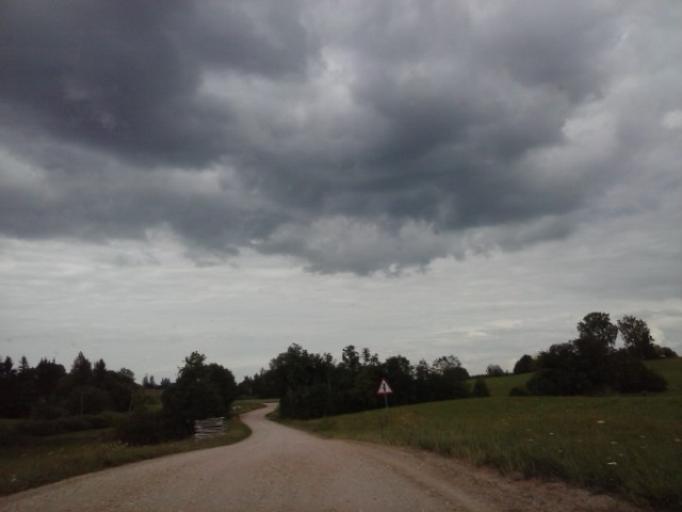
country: EE
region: Vorumaa
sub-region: Voru linn
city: Voru
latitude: 57.7473
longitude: 27.1367
